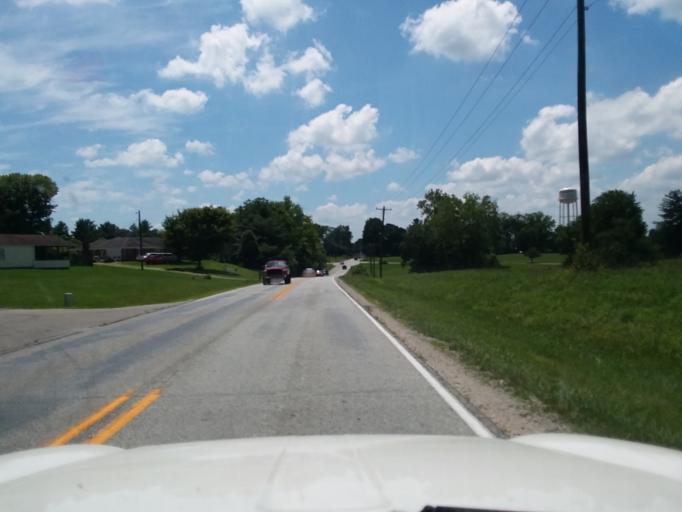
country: US
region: Indiana
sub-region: Johnson County
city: Trafalgar
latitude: 39.3740
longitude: -86.2527
